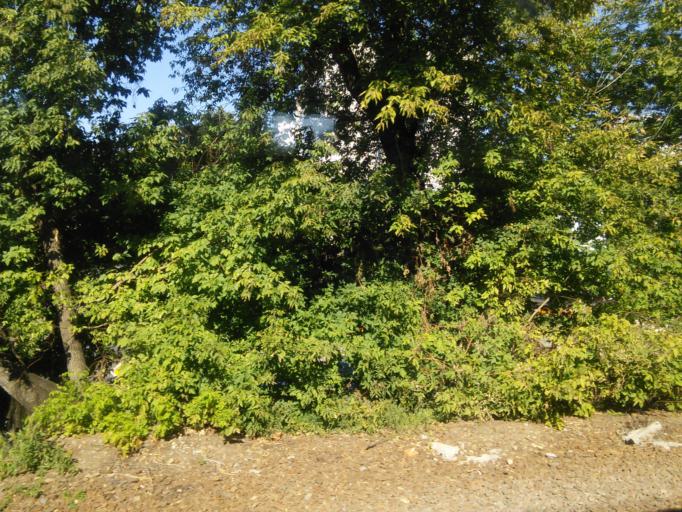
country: RU
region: Moscow
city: Taganskiy
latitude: 55.7496
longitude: 37.6765
